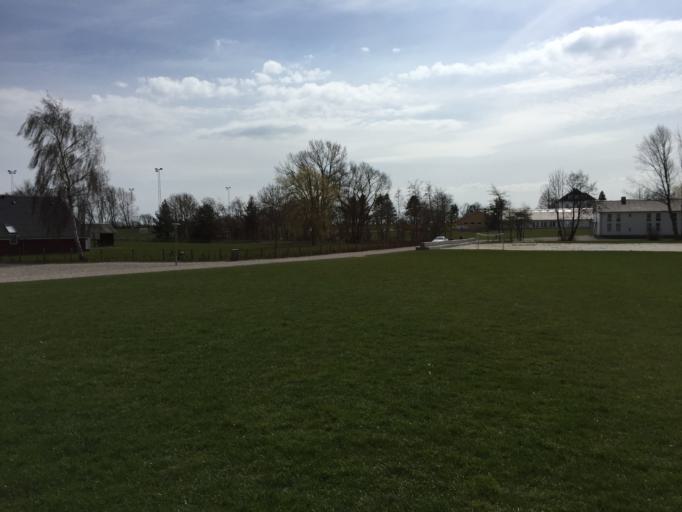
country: DK
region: South Denmark
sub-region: Svendborg Kommune
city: Thuro By
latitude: 55.1154
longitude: 10.7228
